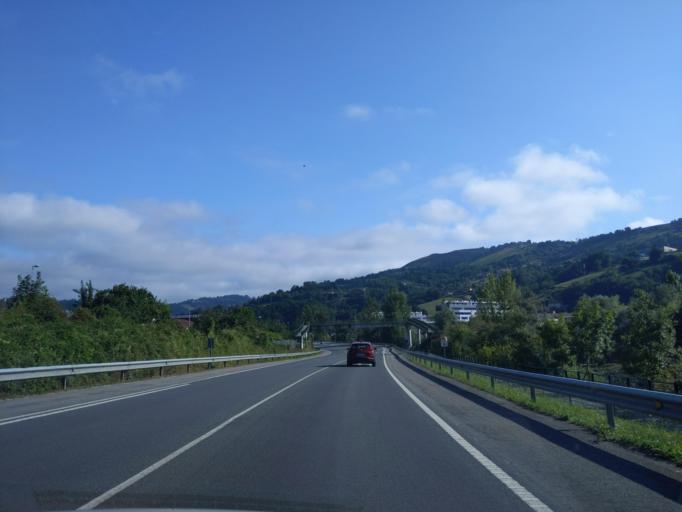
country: ES
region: Asturias
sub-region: Province of Asturias
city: Pola de Laviana
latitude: 43.2461
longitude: -5.5682
